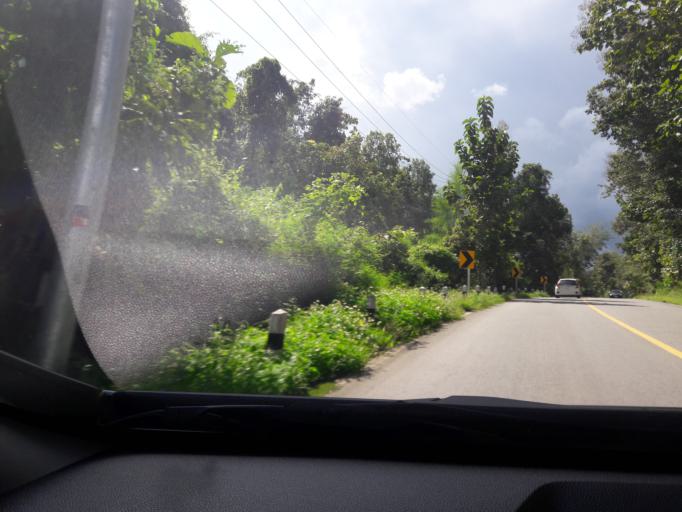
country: TH
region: Mae Hong Son
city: Mae Hi
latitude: 19.3140
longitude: 98.4480
